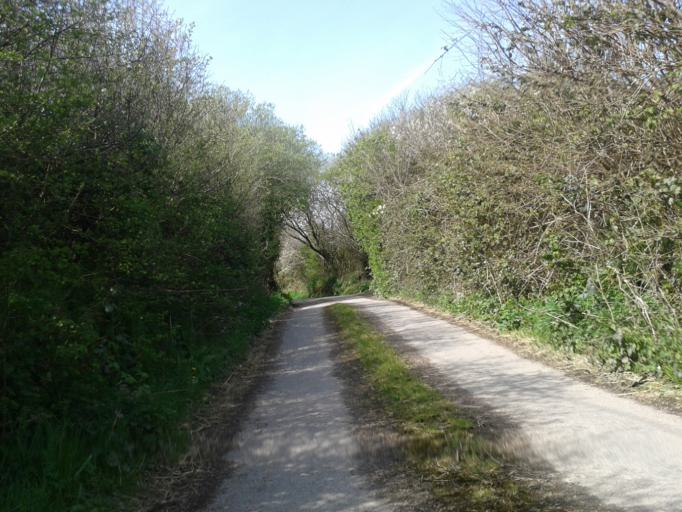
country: GB
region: England
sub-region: Devon
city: Braunton
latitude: 51.1669
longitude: -4.1628
